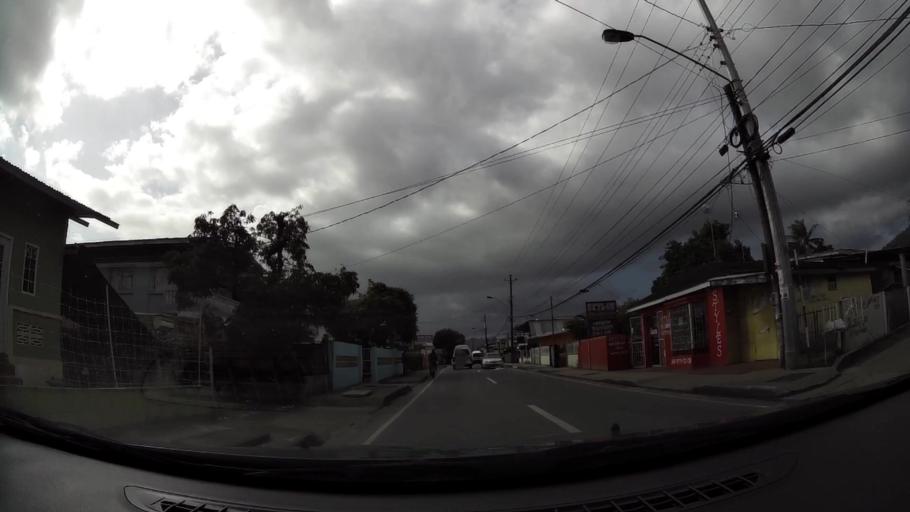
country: TT
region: Tunapuna/Piarco
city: Paradise
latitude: 10.6412
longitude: -61.3535
